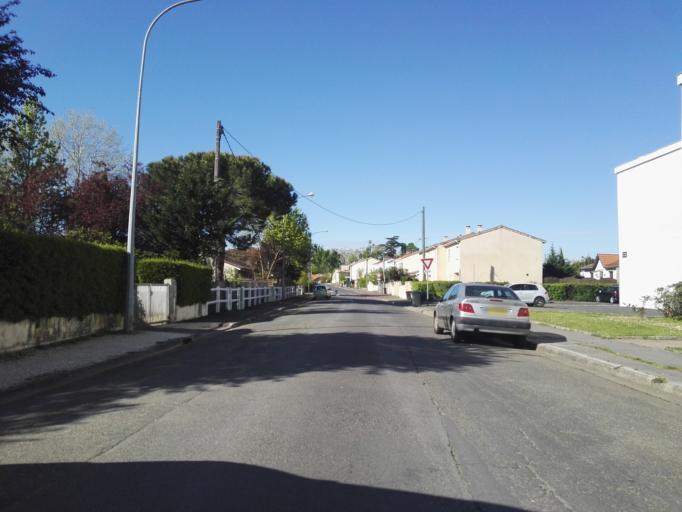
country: FR
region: Aquitaine
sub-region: Departement de la Gironde
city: Talence
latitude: 44.7980
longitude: -0.5851
